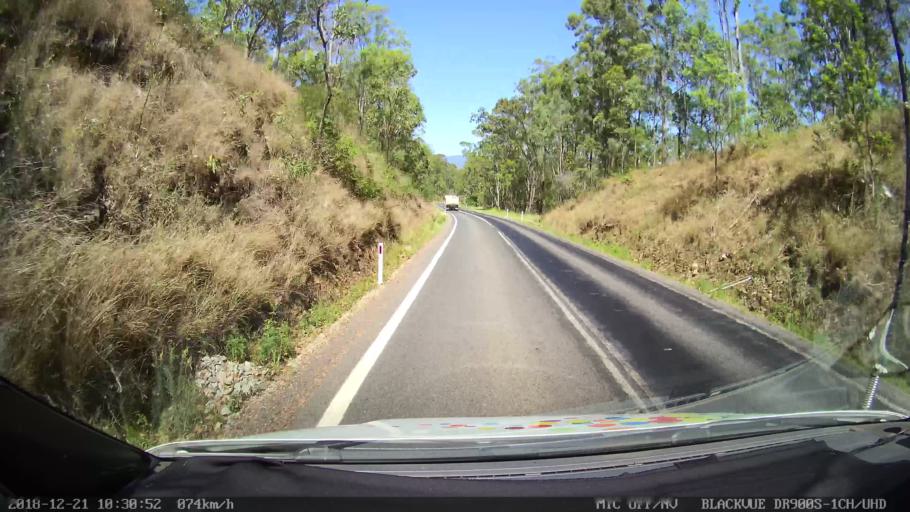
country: AU
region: New South Wales
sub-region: Clarence Valley
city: South Grafton
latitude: -29.6333
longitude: 152.7035
